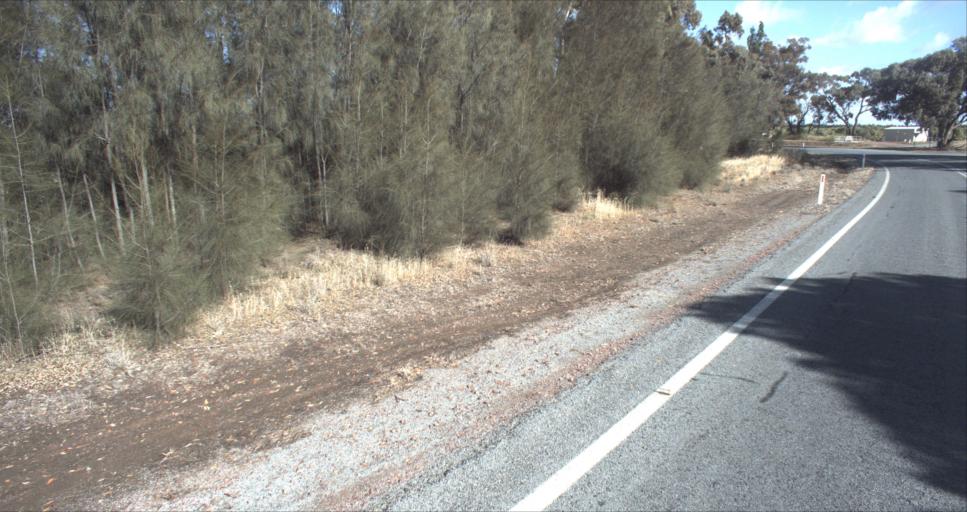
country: AU
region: New South Wales
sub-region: Leeton
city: Leeton
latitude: -34.5457
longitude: 146.3541
